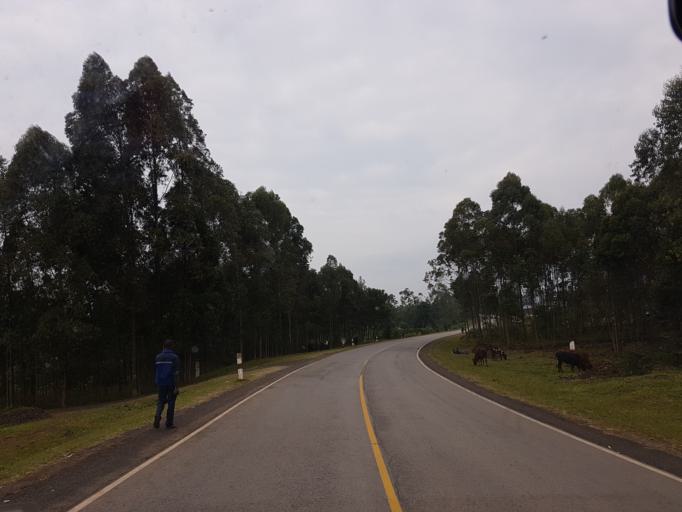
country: UG
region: Western Region
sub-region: Kisoro District
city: Kisoro
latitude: -1.3200
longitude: 29.7278
